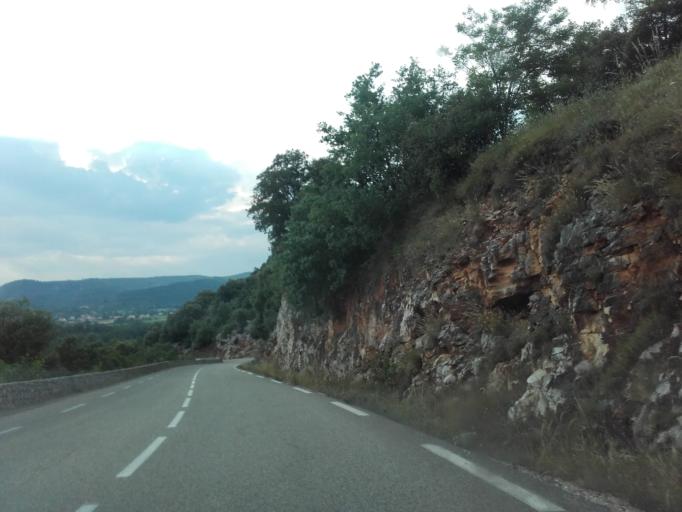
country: FR
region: Rhone-Alpes
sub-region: Departement de l'Ardeche
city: Ruoms
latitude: 44.4017
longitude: 4.4185
